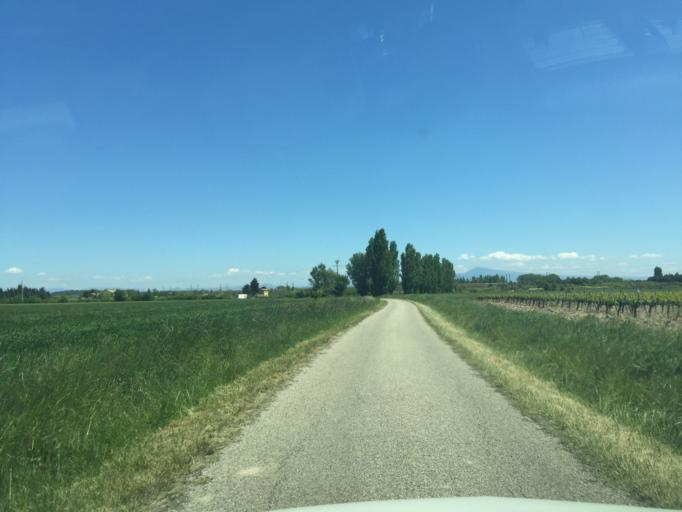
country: FR
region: Provence-Alpes-Cote d'Azur
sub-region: Departement du Vaucluse
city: Caderousse
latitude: 44.0995
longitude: 4.7685
